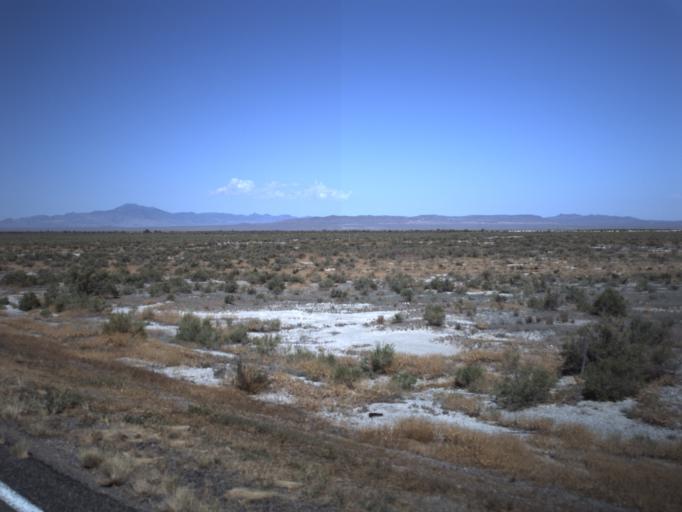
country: US
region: Utah
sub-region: Millard County
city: Delta
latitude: 39.3129
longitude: -112.7632
